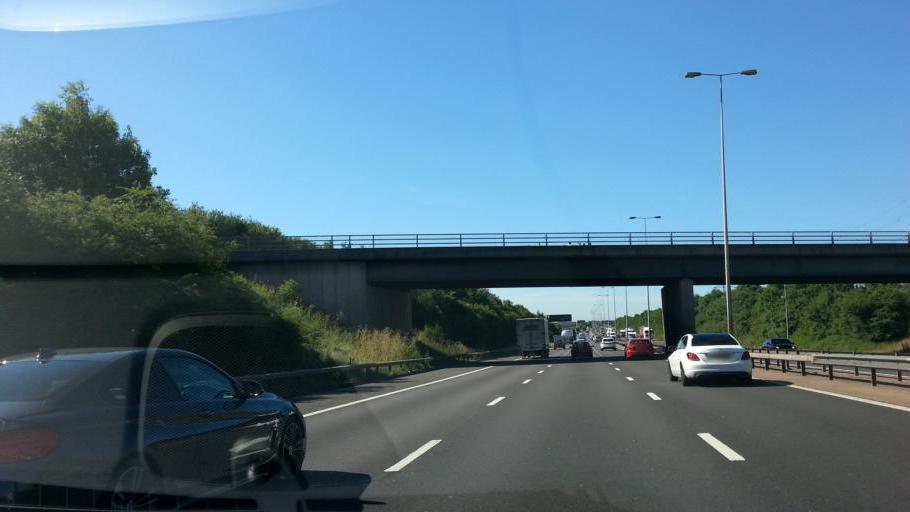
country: GB
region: England
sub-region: Worcestershire
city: Worcester
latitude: 52.1865
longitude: -2.1701
